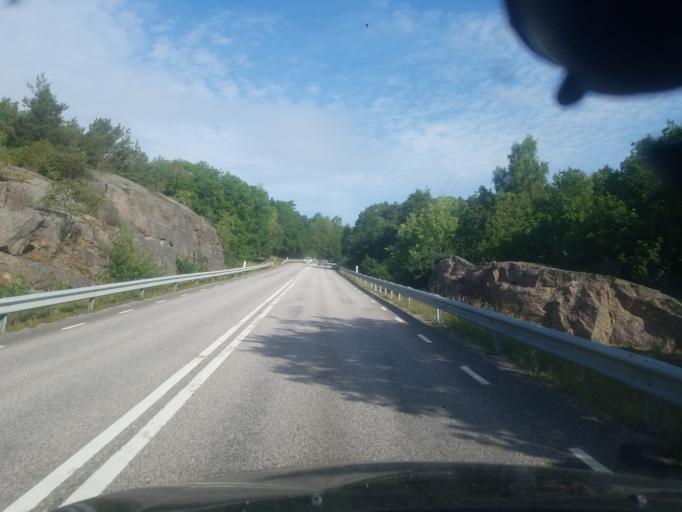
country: SE
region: Vaestra Goetaland
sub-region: Tjorns Kommun
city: Myggenas
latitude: 58.0797
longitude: 11.6958
